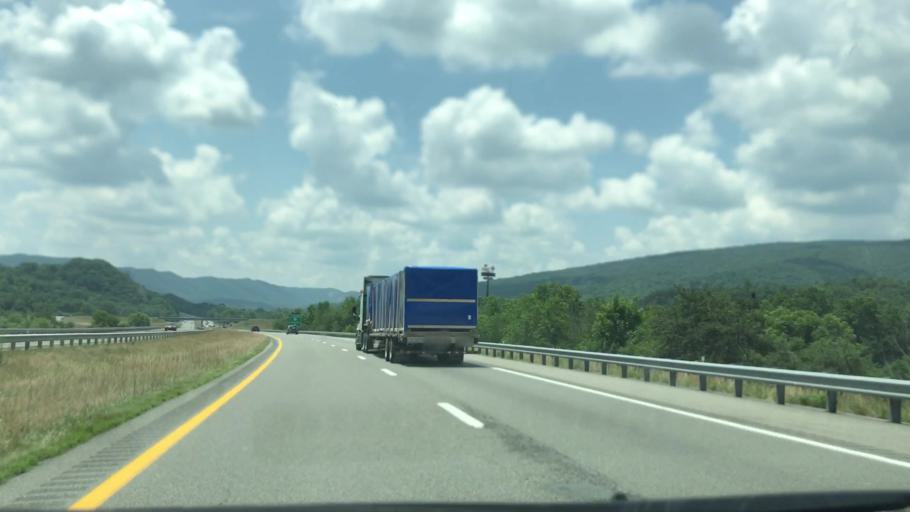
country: US
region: Virginia
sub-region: Bland County
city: Bland
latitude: 37.1829
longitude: -81.1348
